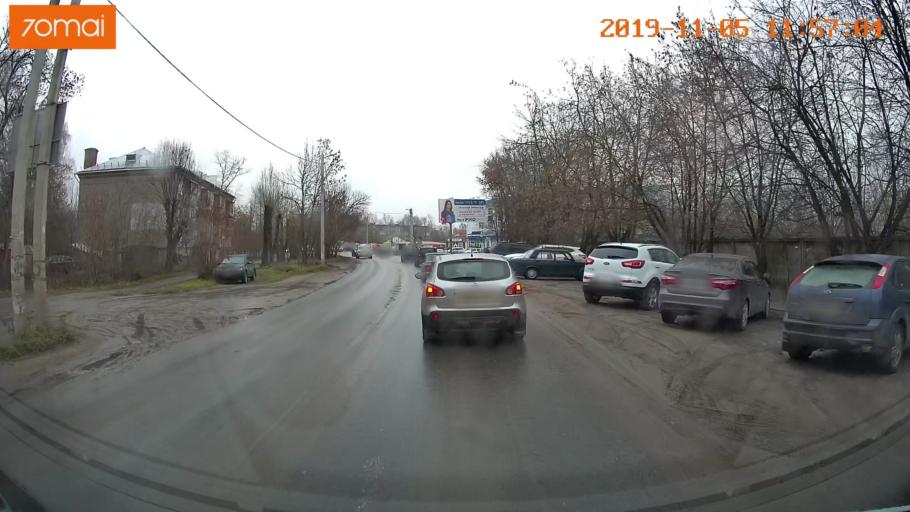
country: RU
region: Ivanovo
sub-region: Gorod Ivanovo
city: Ivanovo
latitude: 56.9842
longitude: 41.0333
